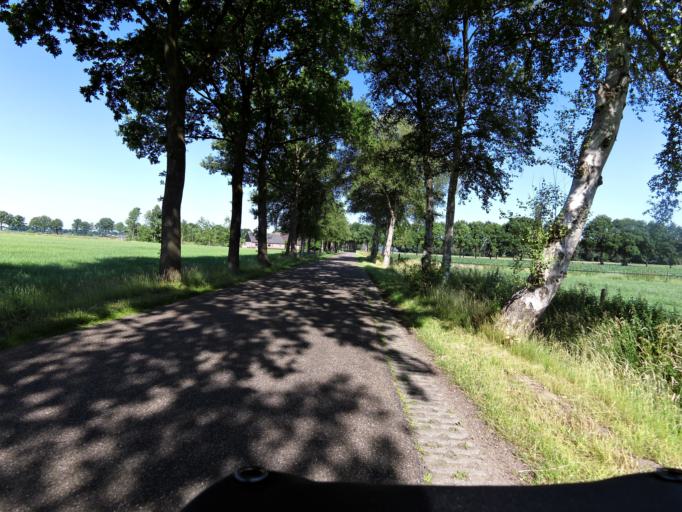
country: NL
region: Overijssel
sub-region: Gemeente Dalfsen
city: Dalfsen
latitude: 52.4807
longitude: 6.3488
